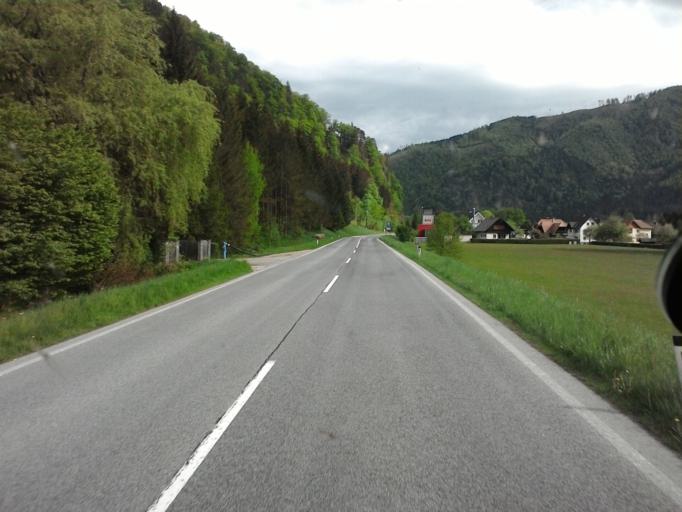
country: AT
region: Styria
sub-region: Politischer Bezirk Liezen
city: Altenmarkt bei Sankt Gallen
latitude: 47.7220
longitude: 14.6523
